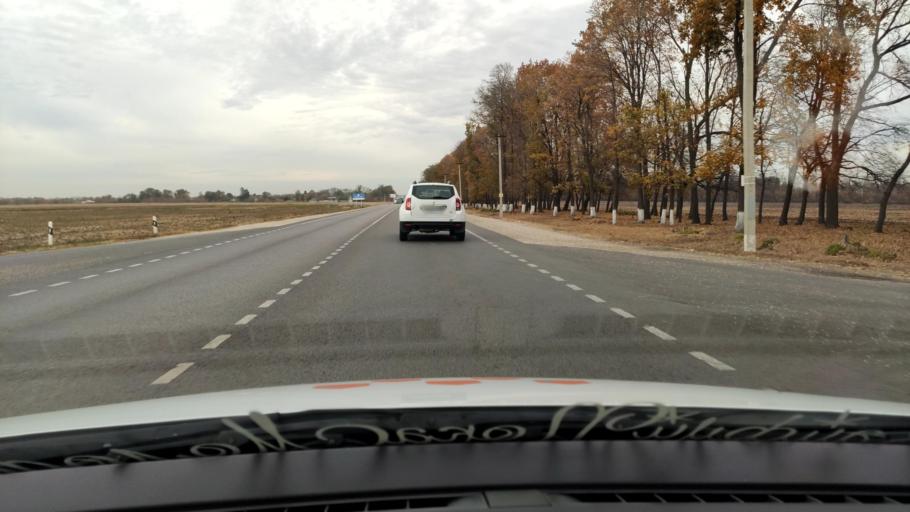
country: RU
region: Voronezj
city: Ramon'
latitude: 51.9247
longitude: 39.2664
